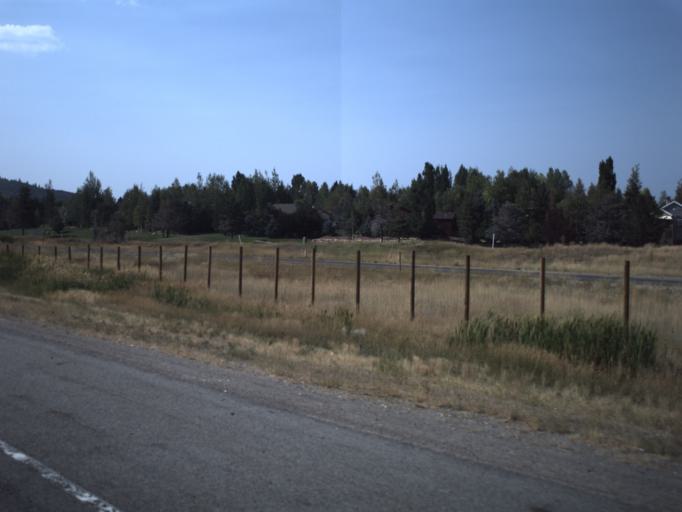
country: US
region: Utah
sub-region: Summit County
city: Summit Park
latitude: 40.7557
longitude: -111.5762
